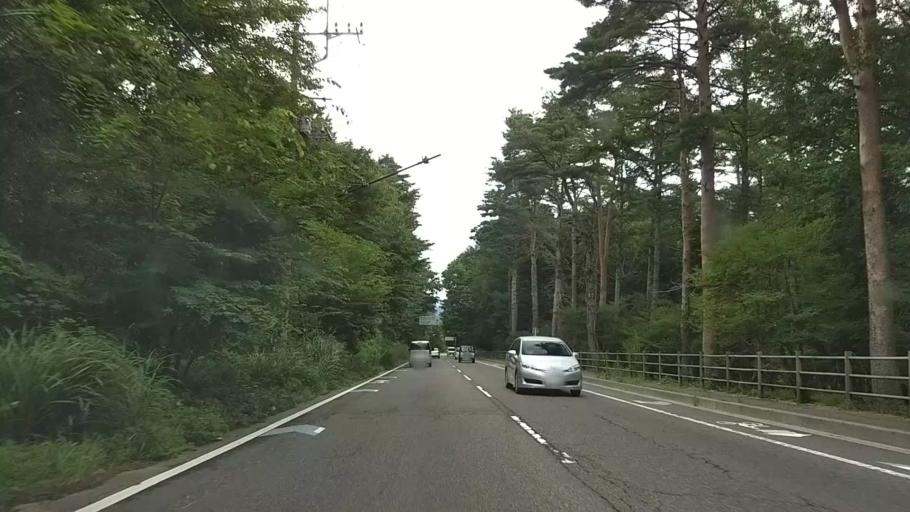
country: JP
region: Yamanashi
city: Fujikawaguchiko
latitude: 35.4465
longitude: 138.8223
